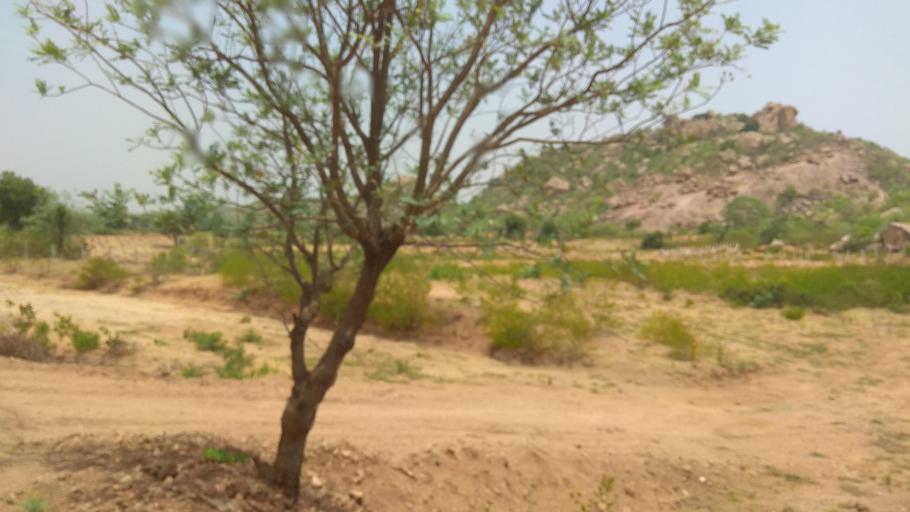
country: IN
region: Telangana
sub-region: Mahbubnagar
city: Farrukhnagar
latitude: 16.8873
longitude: 78.4968
